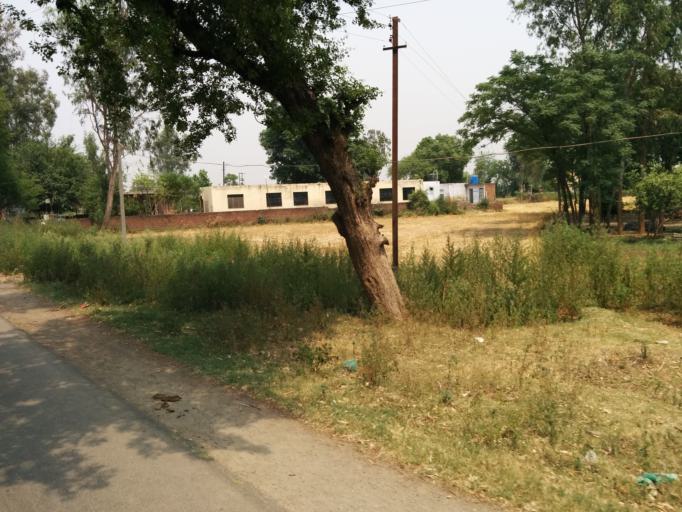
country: IN
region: Punjab
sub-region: Gurdaspur
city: Dhariwal
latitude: 31.9326
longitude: 75.3057
